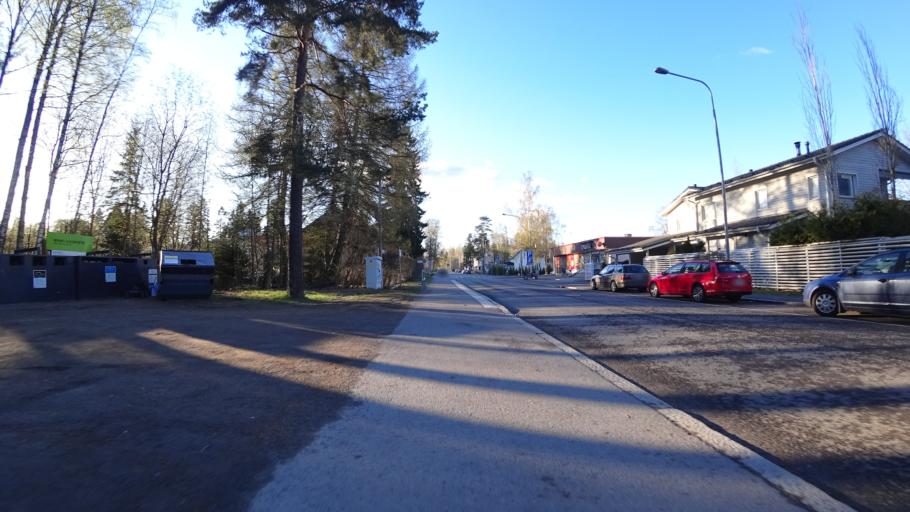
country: FI
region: Pirkanmaa
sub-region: Tampere
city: Pirkkala
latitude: 61.4956
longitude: 23.5852
